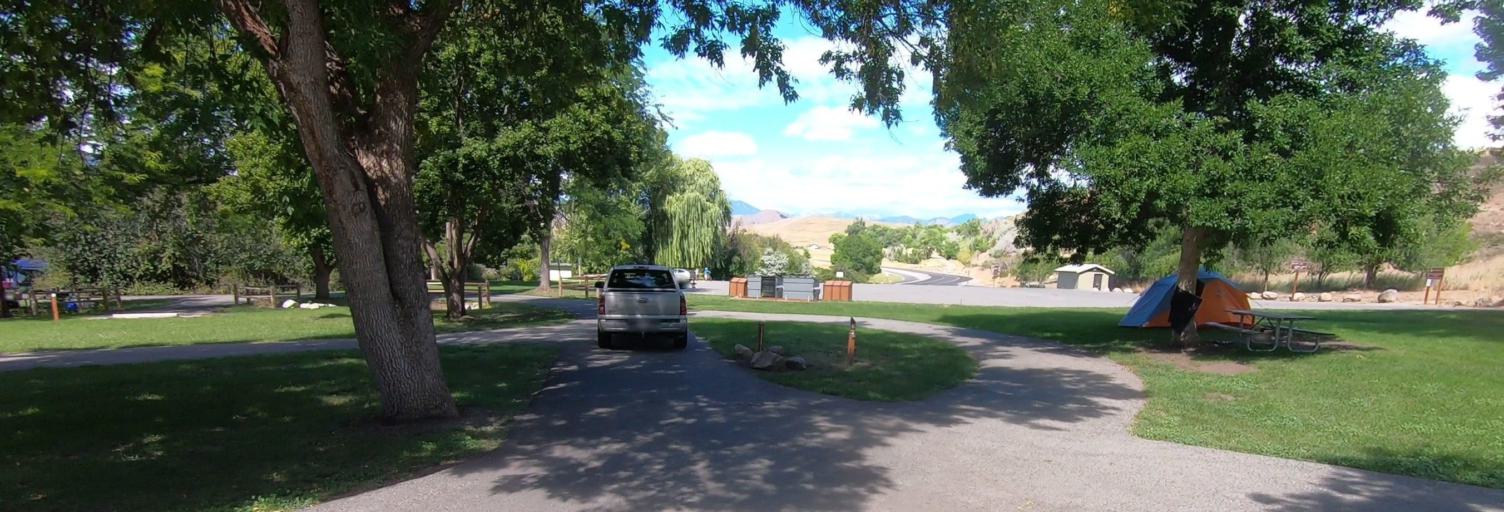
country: US
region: Washington
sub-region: Okanogan County
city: Brewster
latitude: 48.4878
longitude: -120.1475
